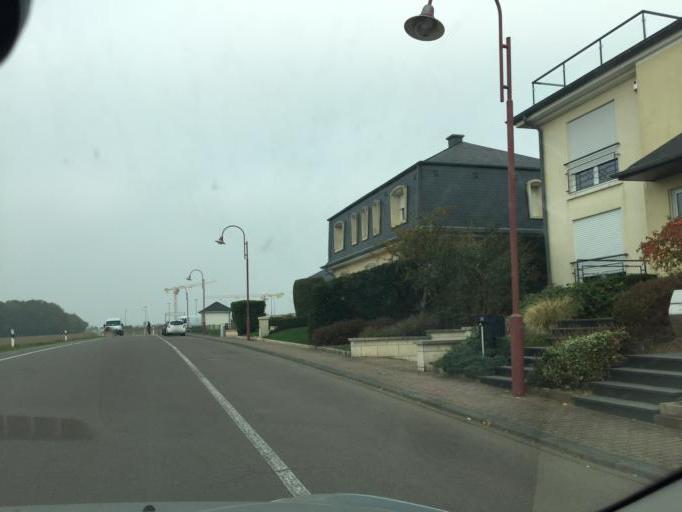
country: LU
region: Luxembourg
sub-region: Canton de Luxembourg
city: Sandweiler
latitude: 49.6130
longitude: 6.2079
